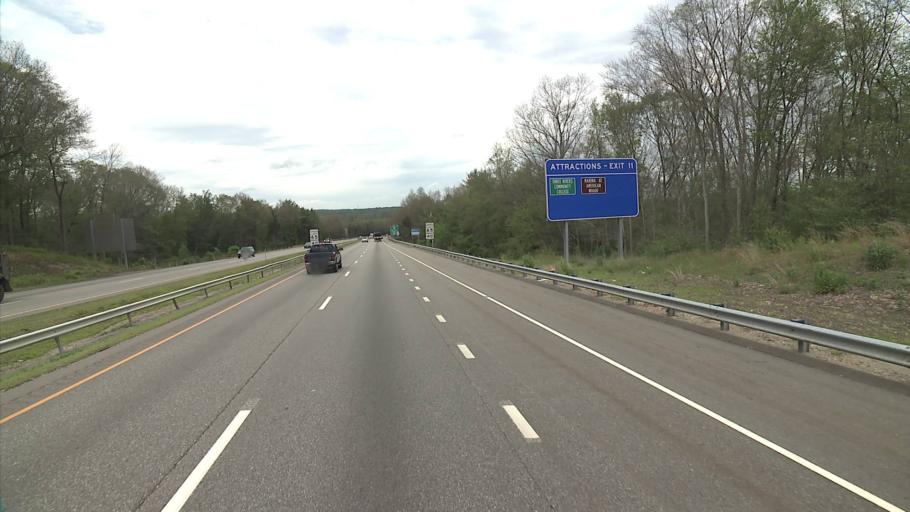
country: US
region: Connecticut
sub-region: New London County
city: Montville Center
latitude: 41.4963
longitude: -72.1152
